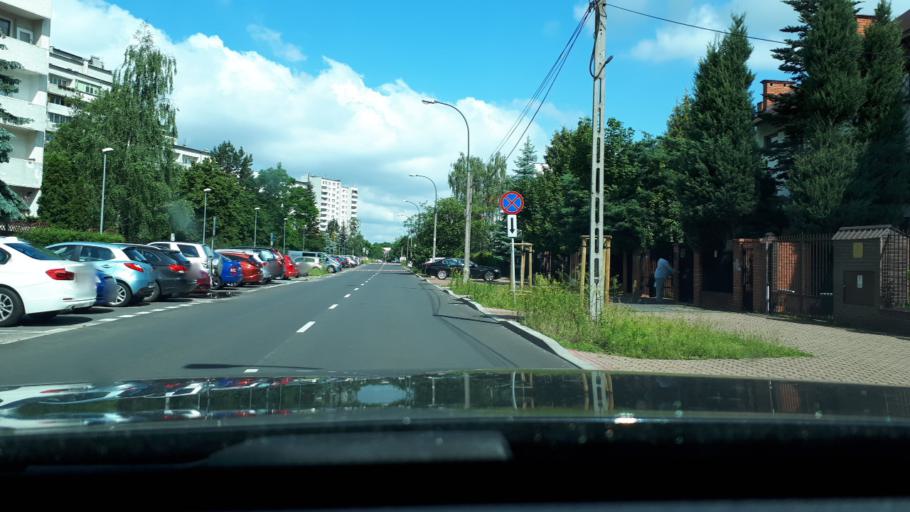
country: PL
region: Masovian Voivodeship
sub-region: Warszawa
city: Wilanow
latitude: 52.1727
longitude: 21.0733
